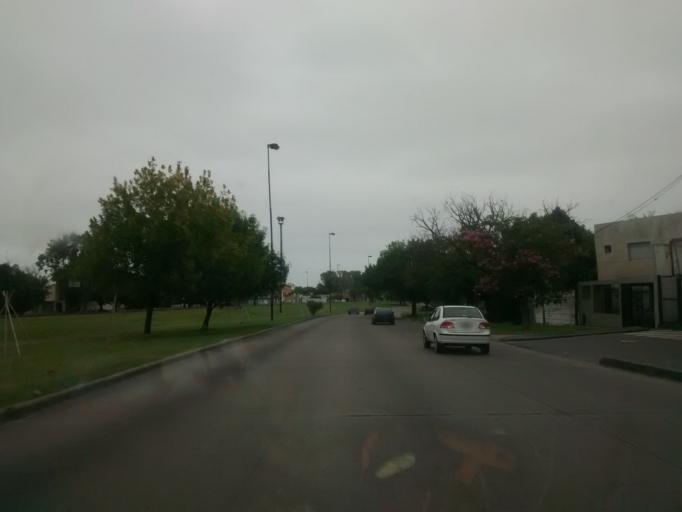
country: AR
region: Buenos Aires
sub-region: Partido de La Plata
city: La Plata
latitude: -34.9498
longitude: -57.9494
